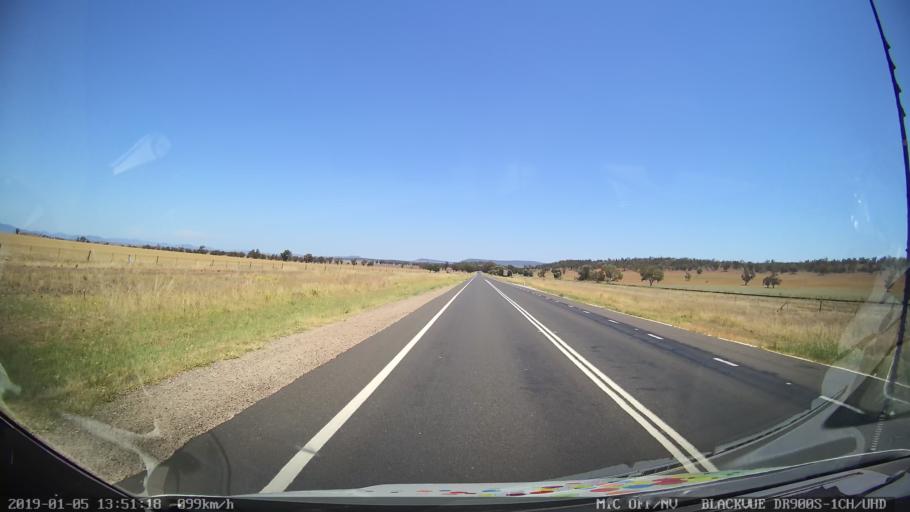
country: AU
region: New South Wales
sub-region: Gunnedah
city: Gunnedah
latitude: -31.0427
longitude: 150.2764
